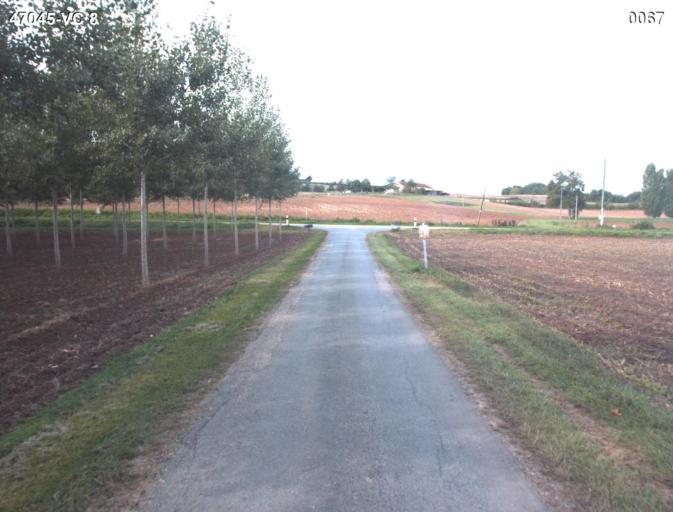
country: FR
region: Aquitaine
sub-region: Departement du Lot-et-Garonne
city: Nerac
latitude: 44.1673
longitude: 0.4202
